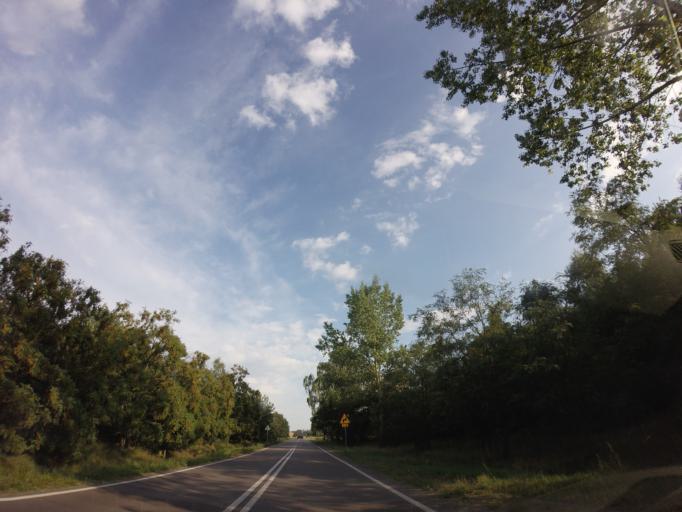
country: PL
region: Lublin Voivodeship
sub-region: Powiat lubartowski
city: Jeziorzany
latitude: 51.5686
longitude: 22.2938
